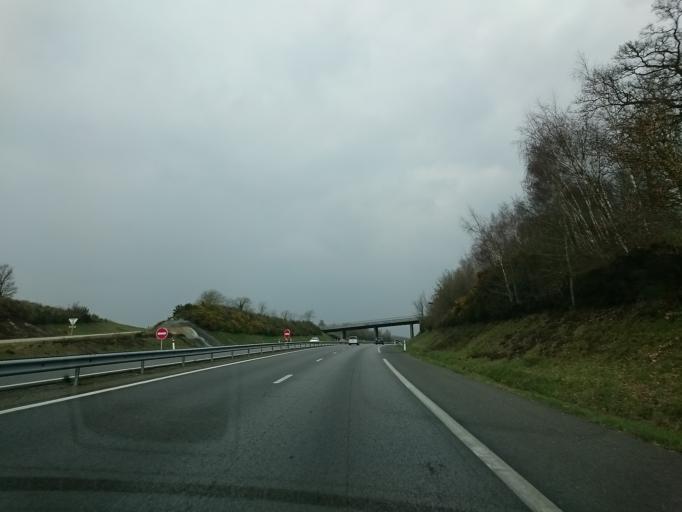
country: FR
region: Brittany
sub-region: Departement d'Ille-et-Vilaine
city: Pance
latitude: 47.8880
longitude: -1.6902
